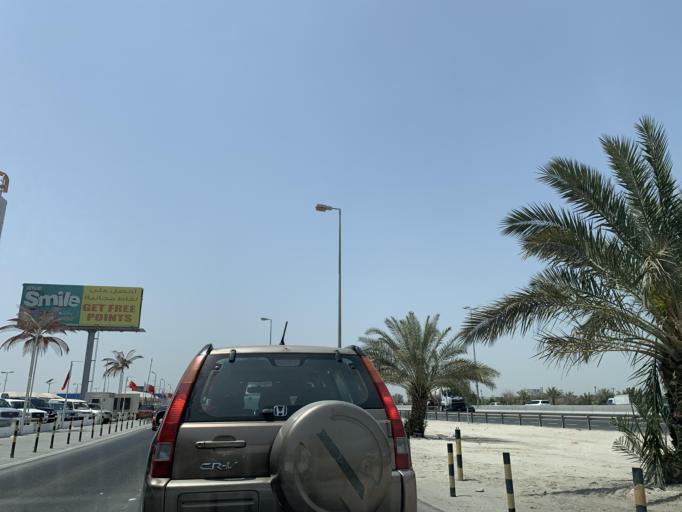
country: BH
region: Manama
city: Jidd Hafs
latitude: 26.1963
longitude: 50.5451
